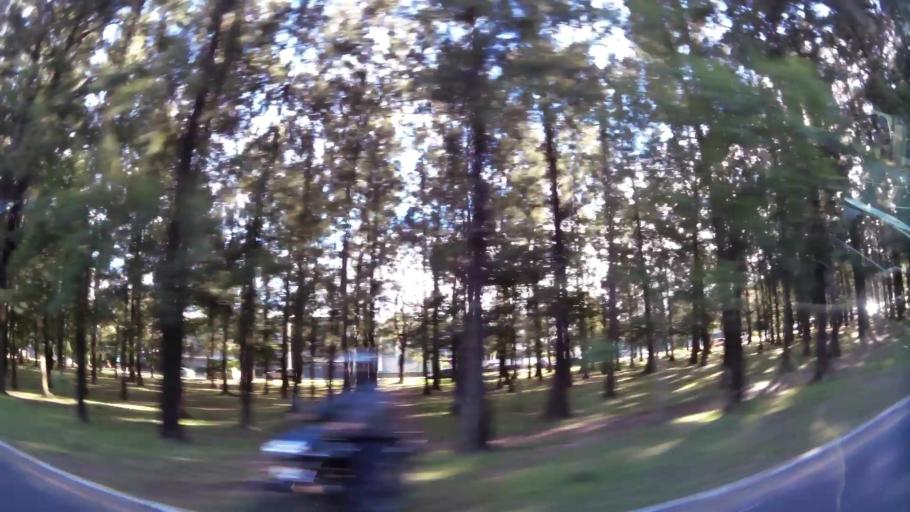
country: GT
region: Guatemala
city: Santa Catarina Pinula
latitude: 14.6021
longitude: -90.5004
